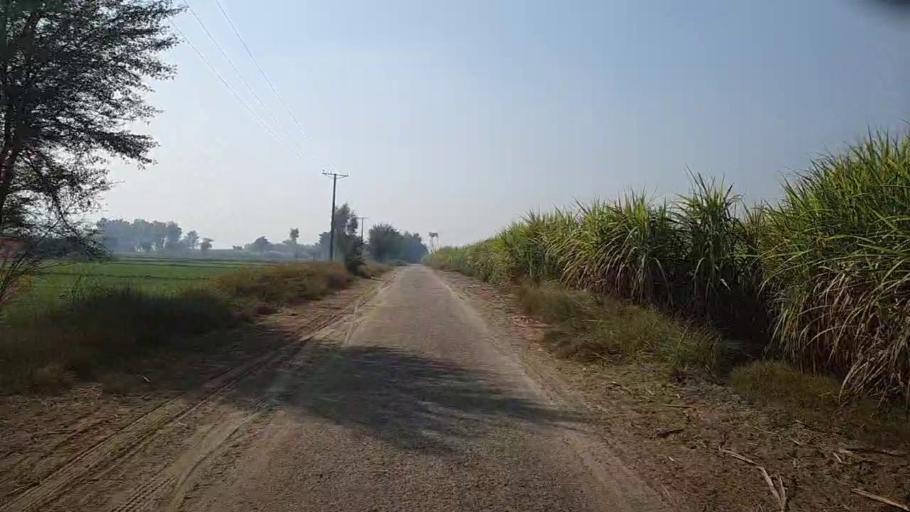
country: PK
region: Sindh
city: Bozdar
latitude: 27.2656
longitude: 68.6236
